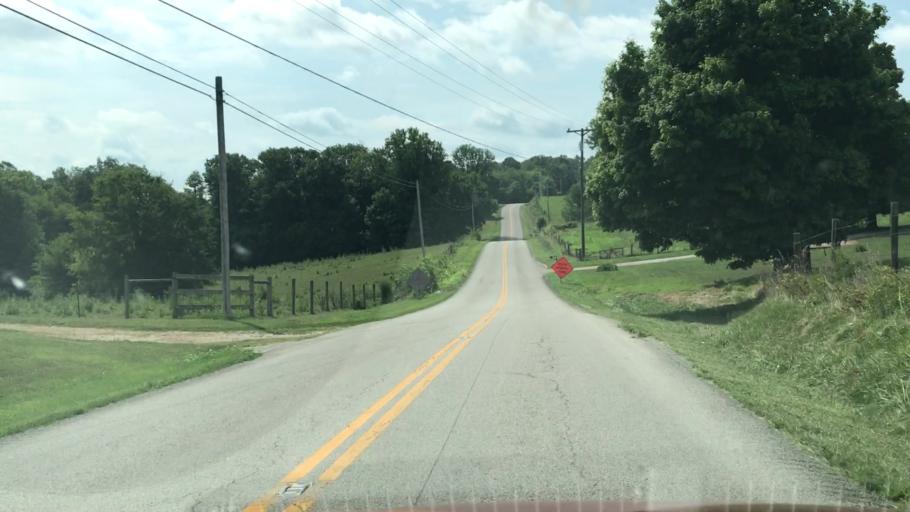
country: US
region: Kentucky
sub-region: Barren County
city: Glasgow
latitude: 36.9048
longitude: -85.8671
